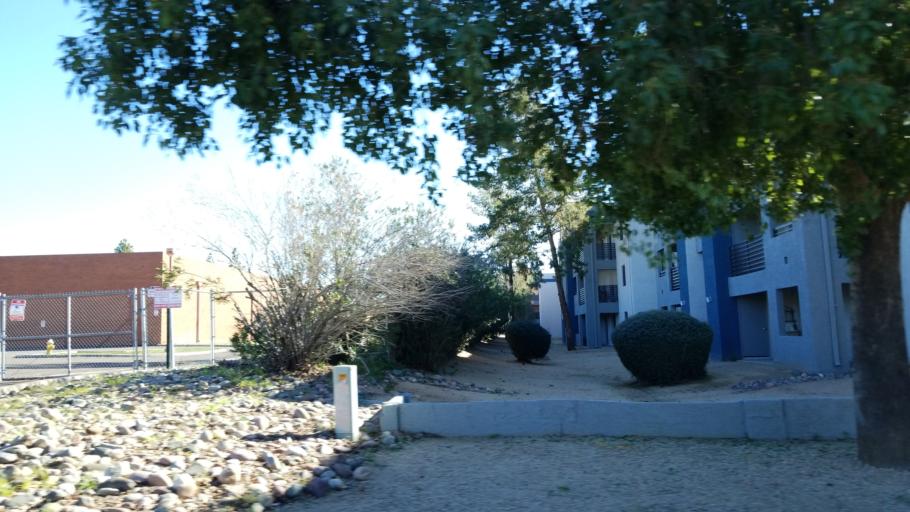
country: US
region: Arizona
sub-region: Maricopa County
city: Glendale
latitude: 33.6493
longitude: -112.1171
